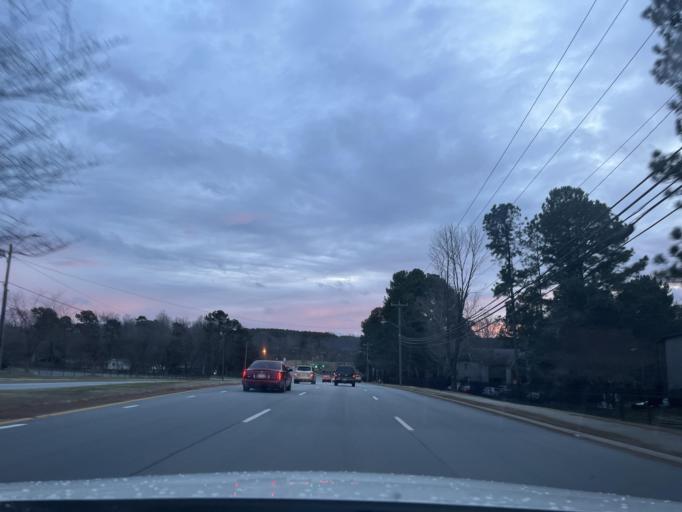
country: US
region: North Carolina
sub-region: Guilford County
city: Greensboro
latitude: 36.0352
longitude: -79.8500
